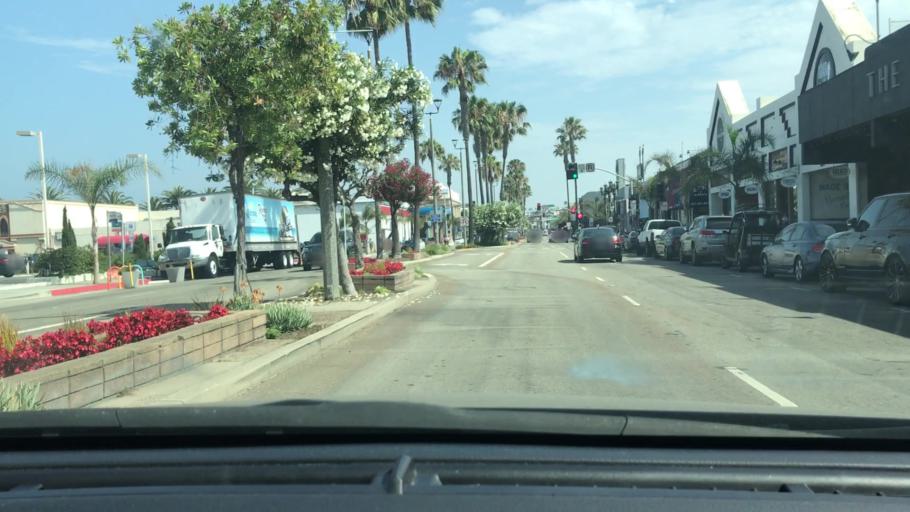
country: US
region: California
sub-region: Los Angeles County
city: Hermosa Beach
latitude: 33.8609
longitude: -118.3996
